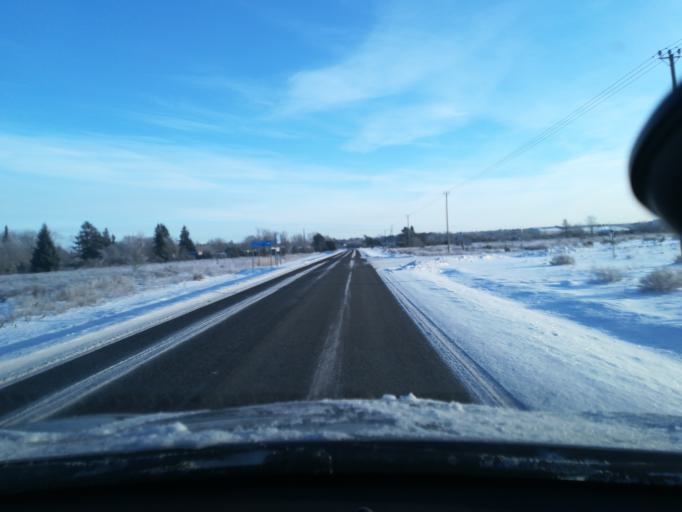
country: EE
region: Harju
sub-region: Keila linn
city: Keila
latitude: 59.3907
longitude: 24.3963
